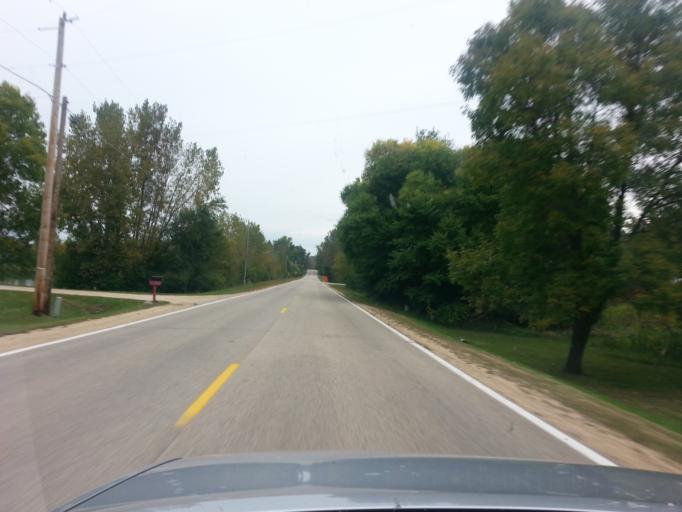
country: US
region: Minnesota
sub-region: Washington County
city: Lake Elmo
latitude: 44.9531
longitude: -92.8428
